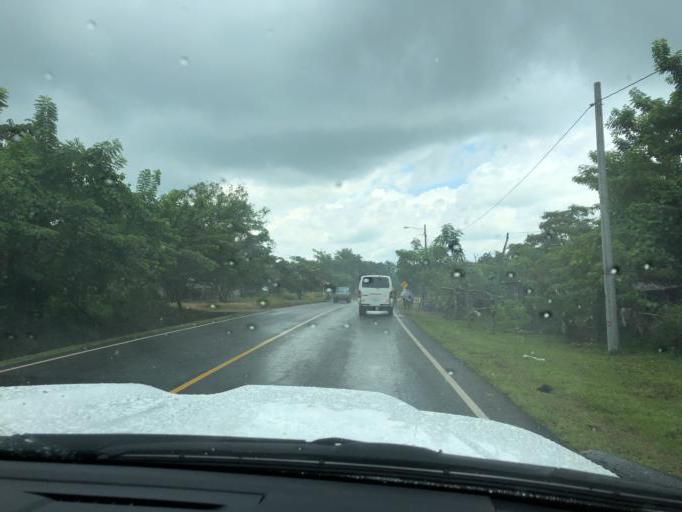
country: NI
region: Chontales
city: Villa Sandino
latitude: 12.0245
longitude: -84.9575
